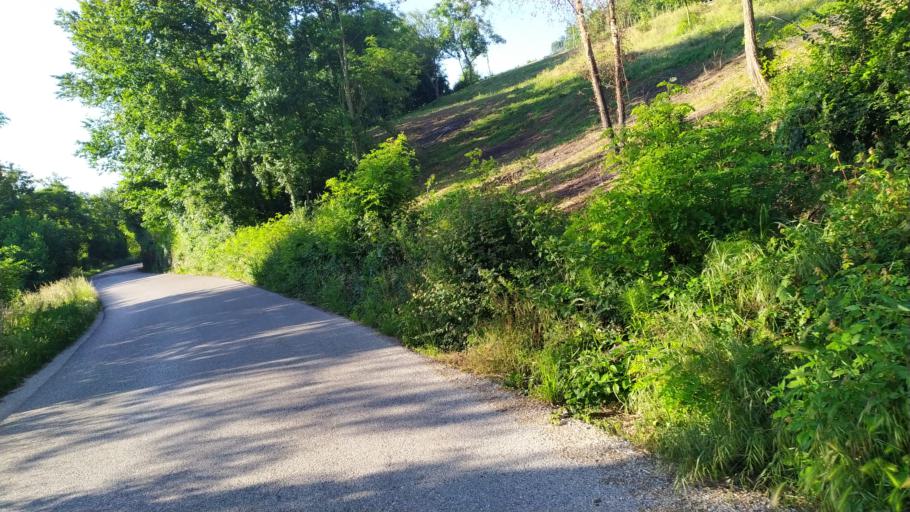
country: IT
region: Veneto
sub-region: Provincia di Vicenza
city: Malo
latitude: 45.6473
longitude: 11.4169
